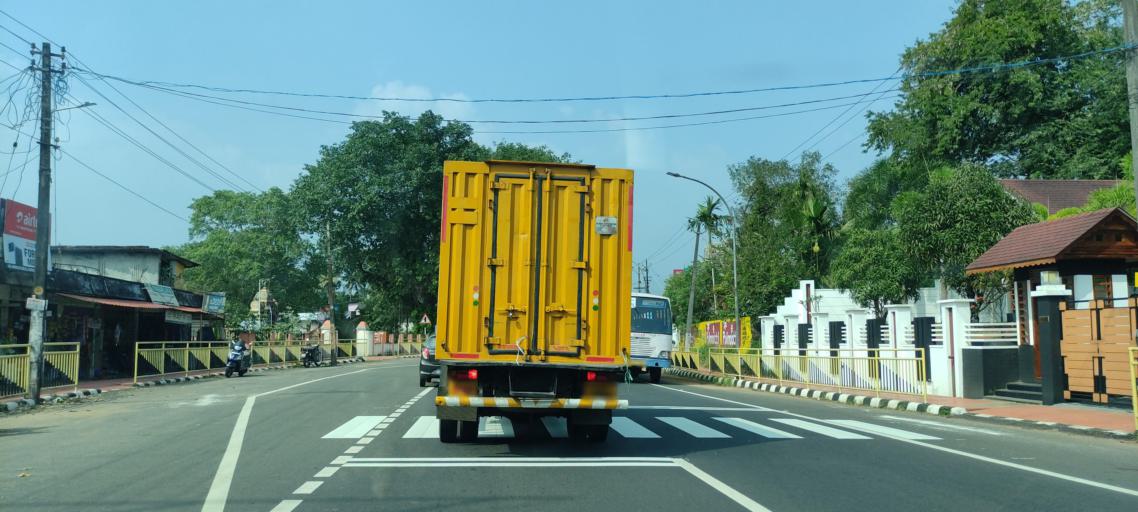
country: IN
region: Kerala
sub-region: Alappuzha
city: Chengannur
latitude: 9.2718
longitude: 76.6551
